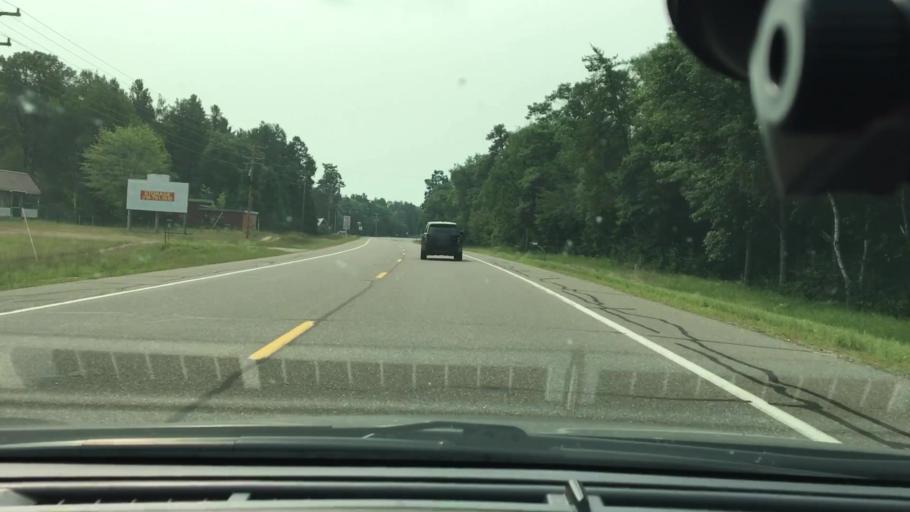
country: US
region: Minnesota
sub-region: Crow Wing County
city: Cross Lake
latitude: 46.5760
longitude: -94.1309
